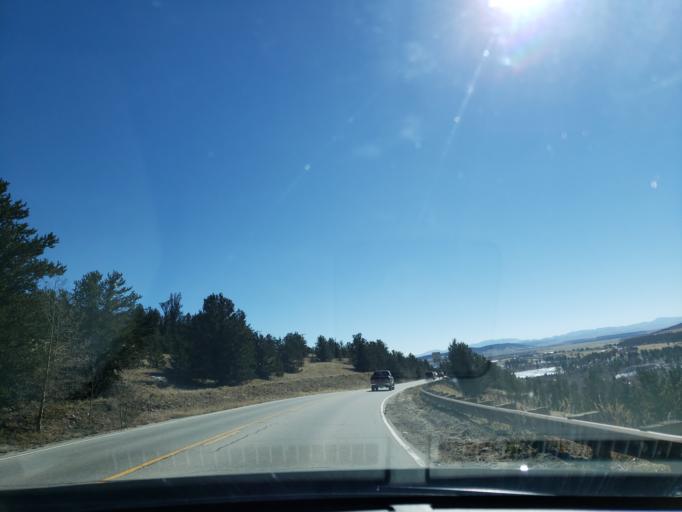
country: US
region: Colorado
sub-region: Park County
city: Fairplay
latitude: 39.2310
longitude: -106.0119
